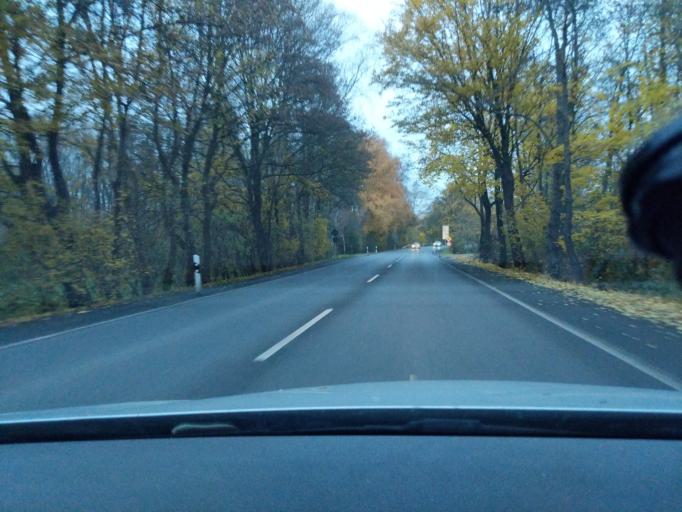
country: DE
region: North Rhine-Westphalia
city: Waltrop
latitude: 51.6263
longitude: 7.4466
